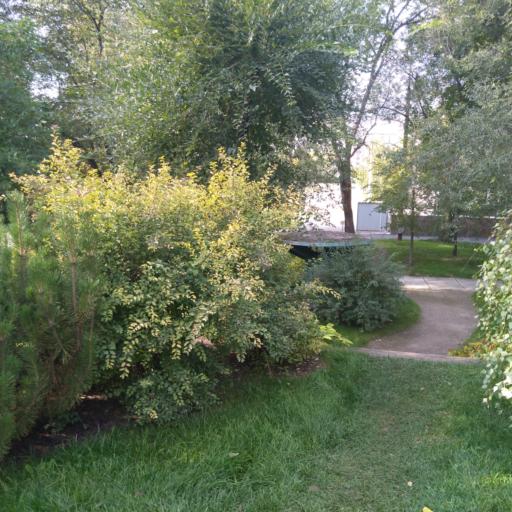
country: RU
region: Krasnoyarskiy
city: Krasnoyarsk
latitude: 56.0151
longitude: 92.9643
